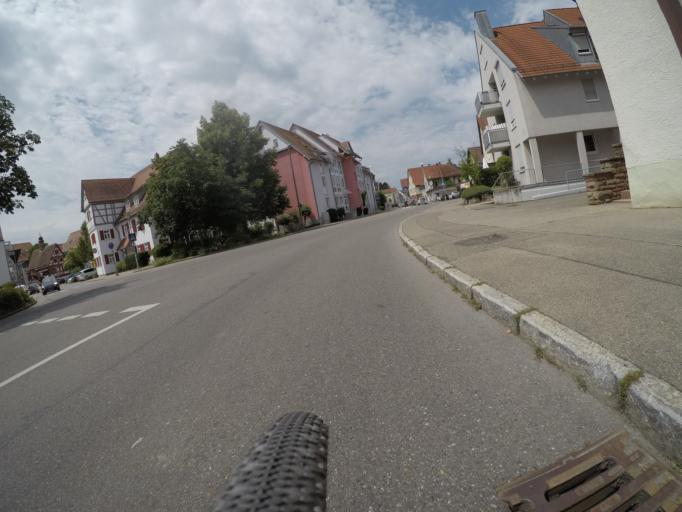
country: DE
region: Baden-Wuerttemberg
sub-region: Regierungsbezirk Stuttgart
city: Magstadt
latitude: 48.7253
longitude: 8.9652
